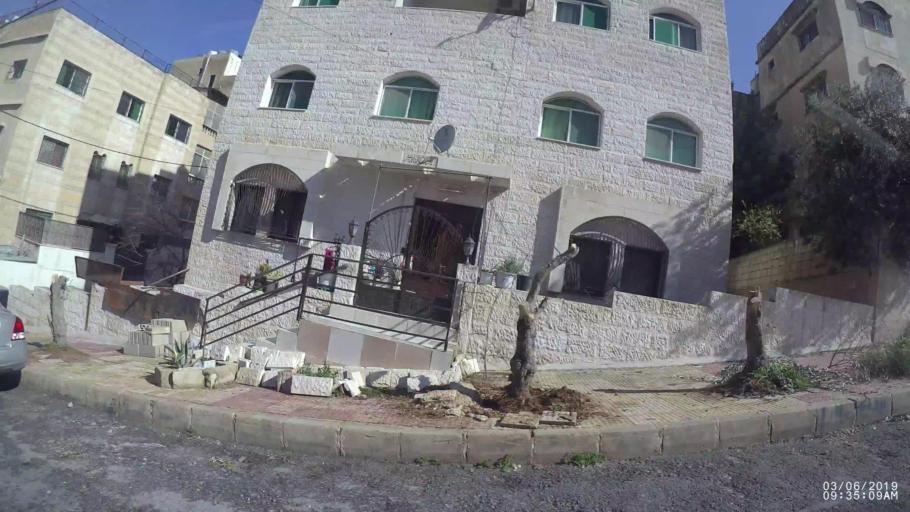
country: JO
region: Amman
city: Amman
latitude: 31.9857
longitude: 35.9863
